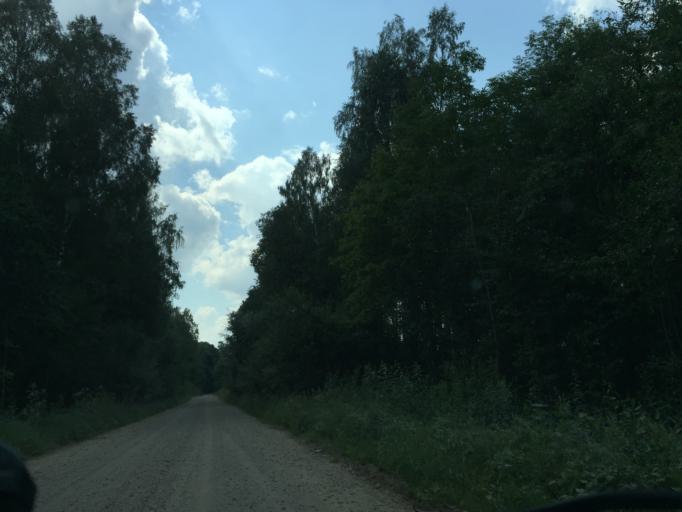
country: LT
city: Zagare
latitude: 56.3761
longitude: 23.1704
